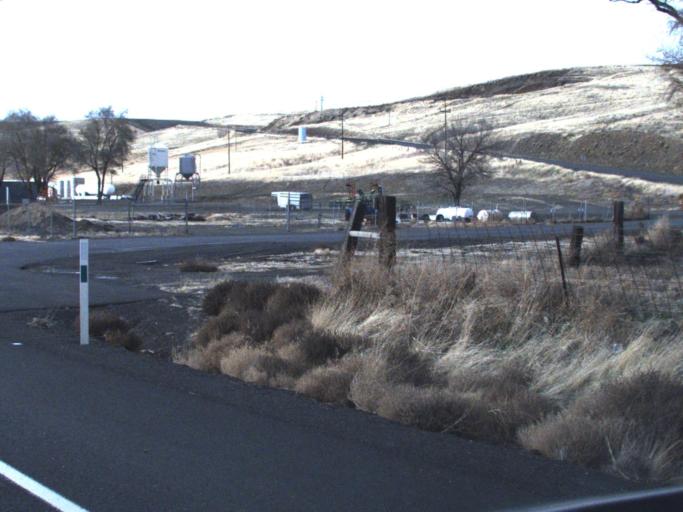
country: US
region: Washington
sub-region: Garfield County
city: Pomeroy
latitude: 46.4748
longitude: -117.5640
